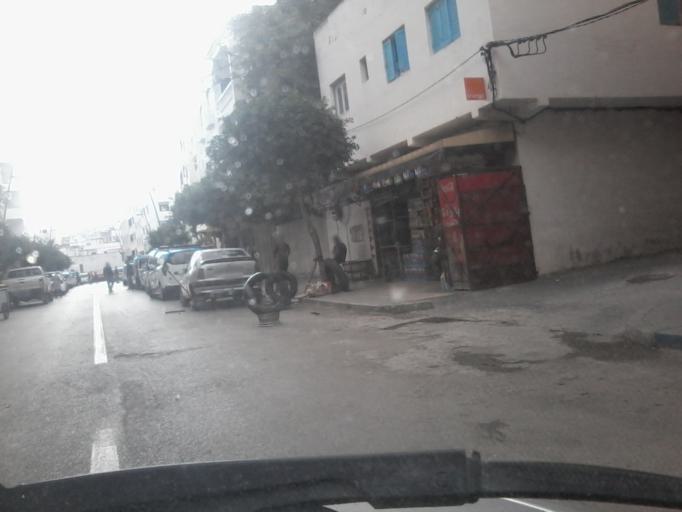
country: MA
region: Tanger-Tetouan
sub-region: Tetouan
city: Martil
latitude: 35.6856
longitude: -5.3243
